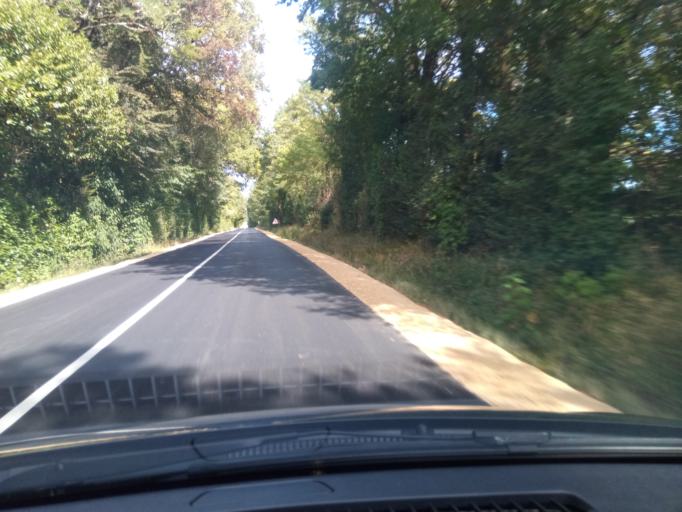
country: FR
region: Poitou-Charentes
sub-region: Departement de la Vienne
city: Terce
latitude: 46.4843
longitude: 0.5355
